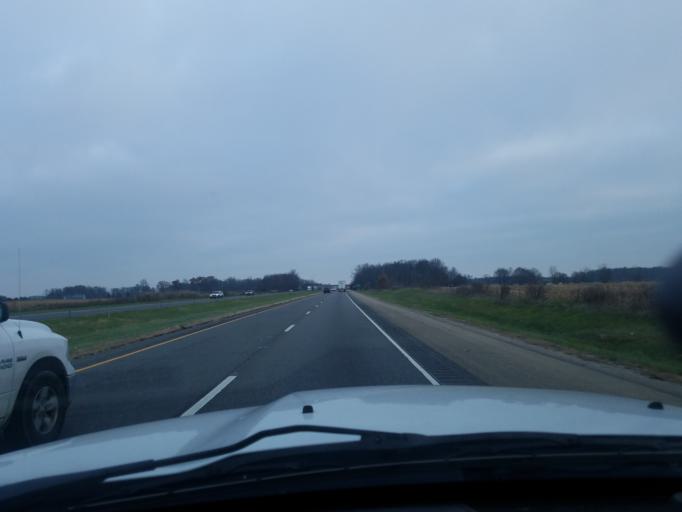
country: US
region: Indiana
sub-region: Delaware County
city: Daleville
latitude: 40.1282
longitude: -85.5685
